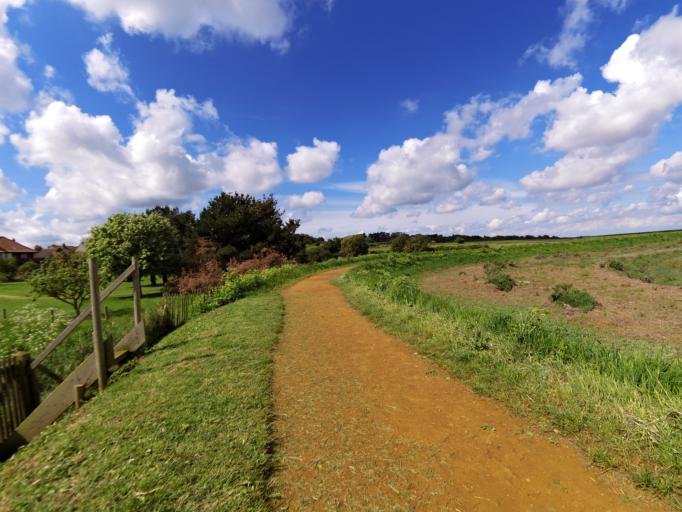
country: GB
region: England
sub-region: Norfolk
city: Briston
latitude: 52.9549
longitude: 1.0109
